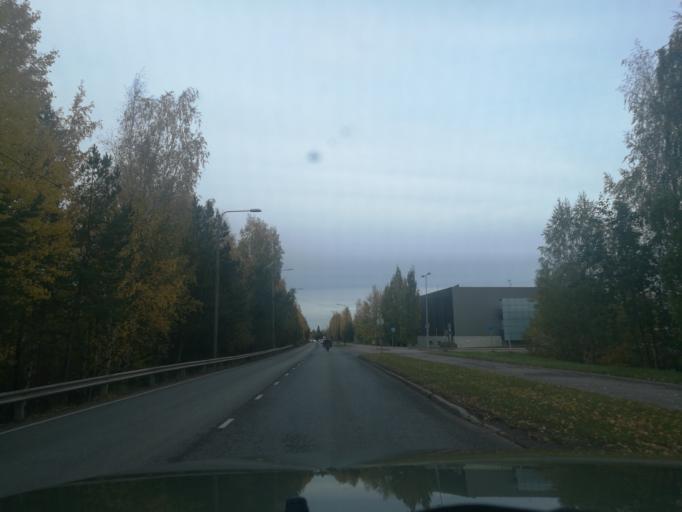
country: FI
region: Uusimaa
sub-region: Helsinki
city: Vantaa
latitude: 60.3000
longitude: 25.0875
